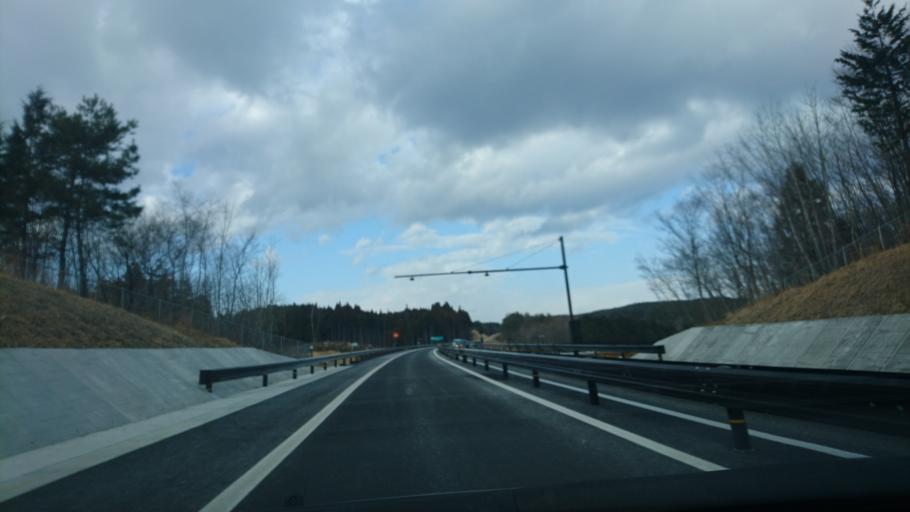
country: JP
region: Miyagi
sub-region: Oshika Gun
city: Onagawa Cho
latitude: 38.7224
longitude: 141.5126
